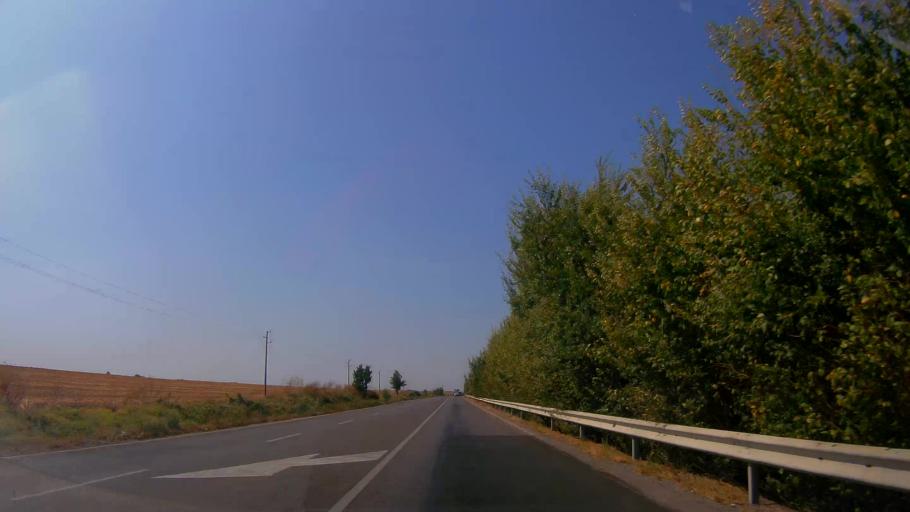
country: BG
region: Ruse
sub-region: Obshtina Vetovo
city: Senovo
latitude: 43.5621
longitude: 26.3497
